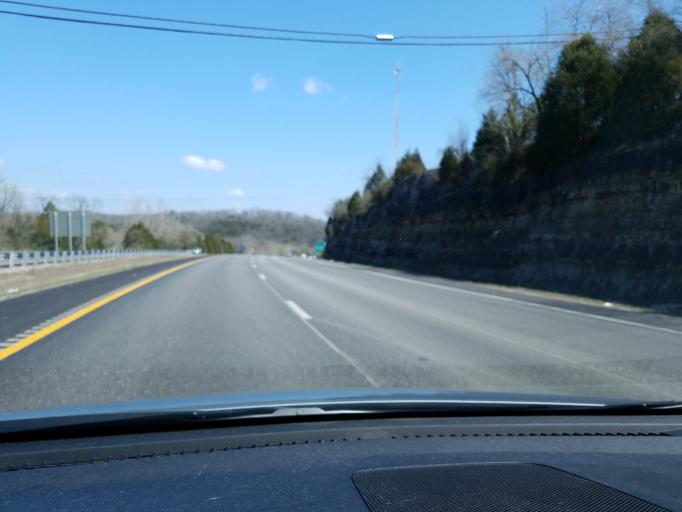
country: US
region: Missouri
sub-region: Taney County
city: Branson
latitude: 36.6445
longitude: -93.2275
